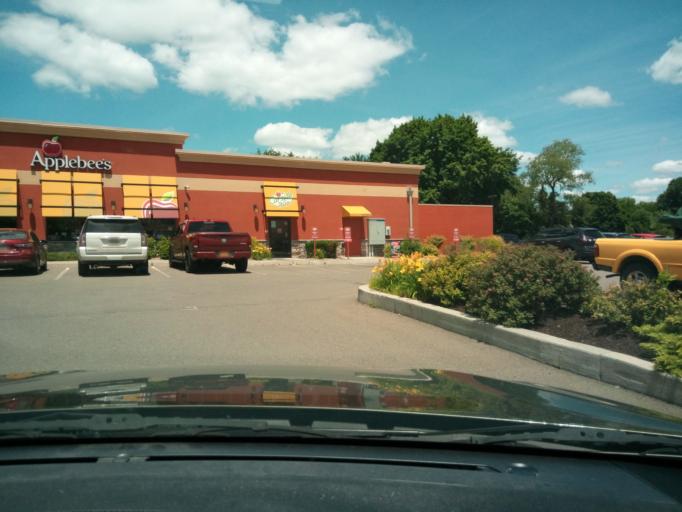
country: US
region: Pennsylvania
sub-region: Bradford County
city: South Waverly
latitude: 41.9752
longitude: -76.5405
